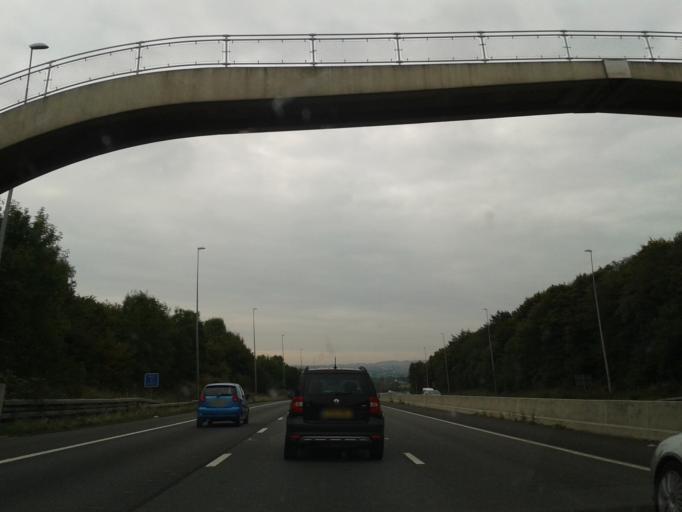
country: GB
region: England
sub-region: Borough of Wigan
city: Shevington
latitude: 53.5828
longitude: -2.6935
